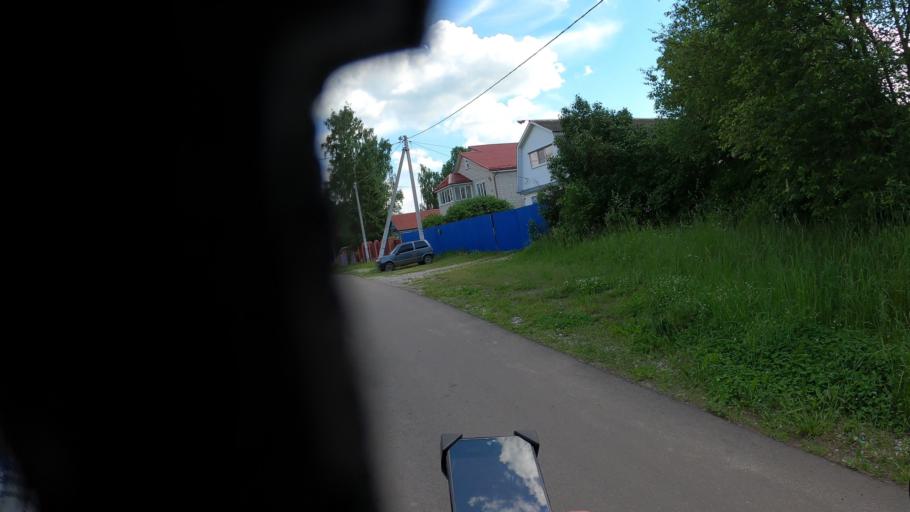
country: RU
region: Moskovskaya
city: Konobeyevo
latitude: 55.3959
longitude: 38.6793
